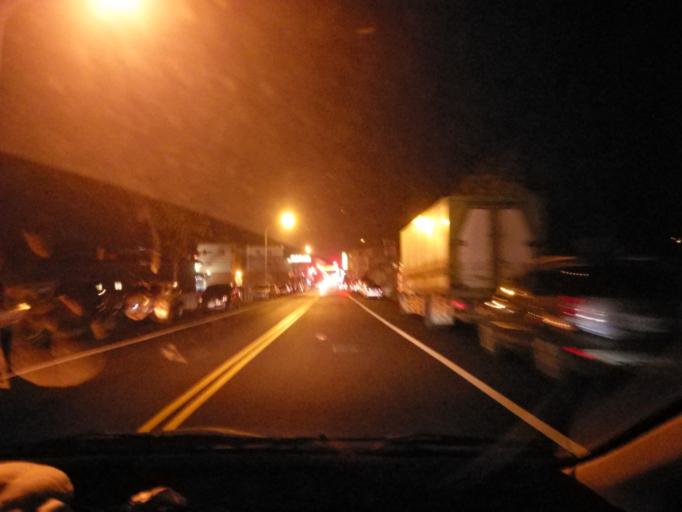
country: TW
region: Taiwan
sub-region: Miaoli
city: Miaoli
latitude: 24.6952
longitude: 120.8692
